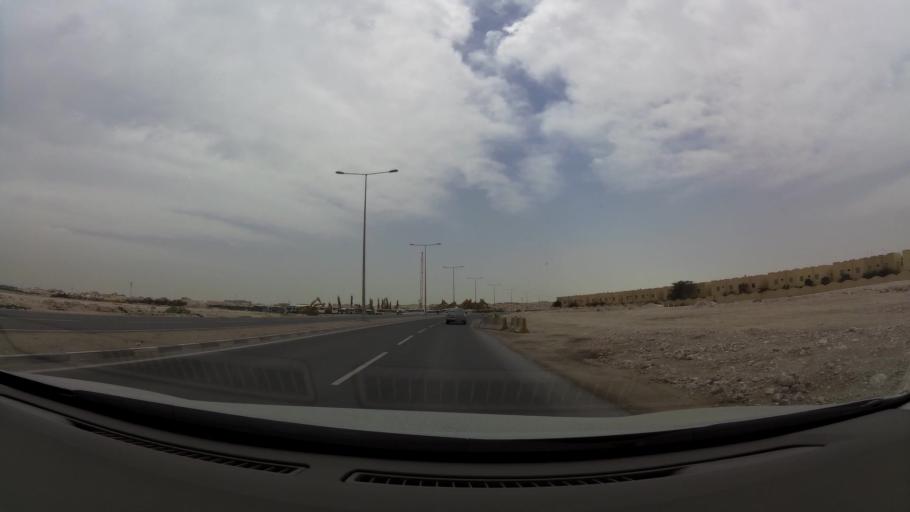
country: QA
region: Baladiyat ad Dawhah
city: Doha
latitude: 25.2333
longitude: 51.4707
